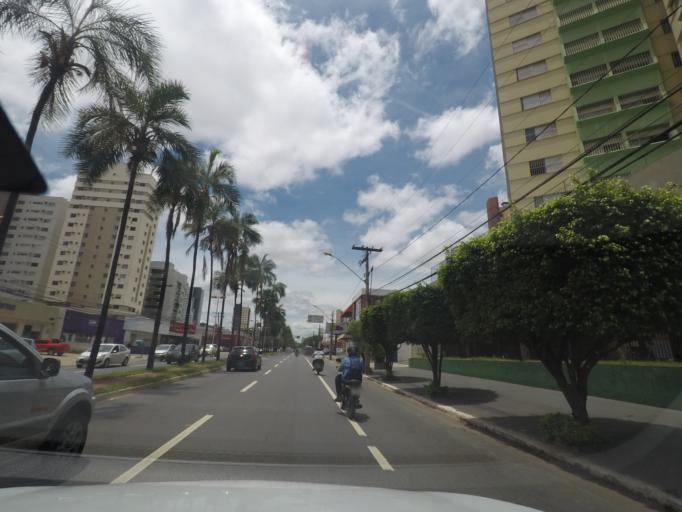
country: BR
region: Goias
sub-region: Goiania
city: Goiania
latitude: -16.6862
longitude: -49.2685
